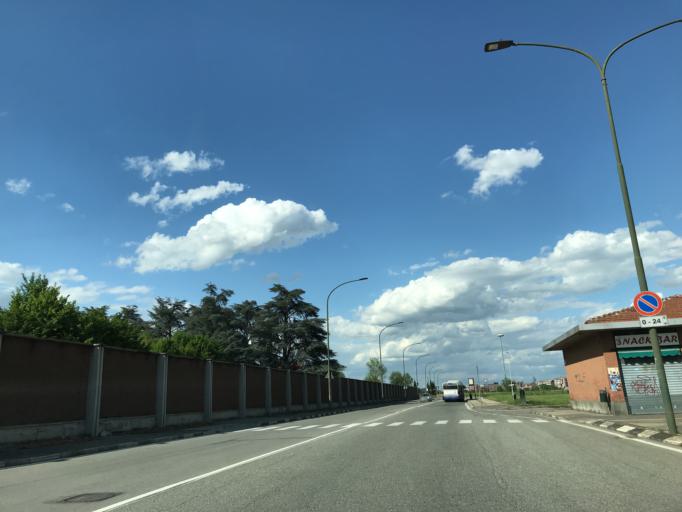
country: IT
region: Piedmont
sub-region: Provincia di Torino
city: Fornaci
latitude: 45.0331
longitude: 7.6043
